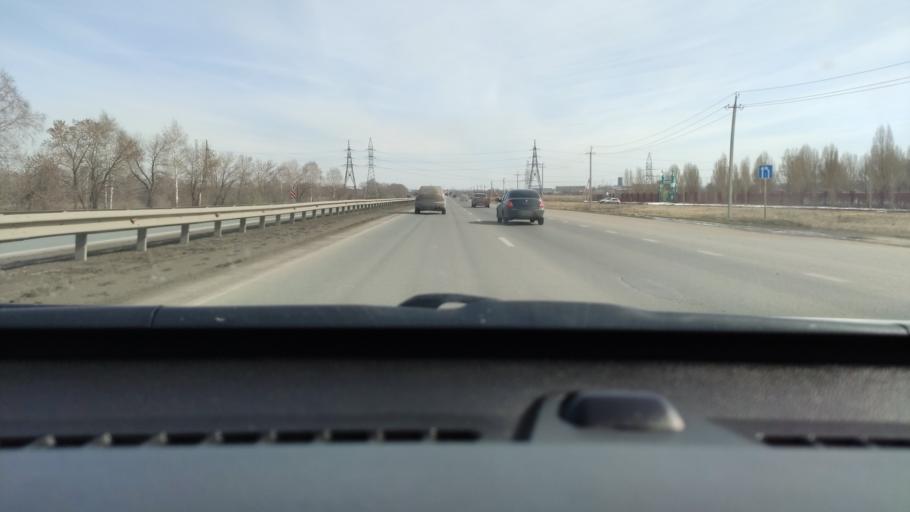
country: RU
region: Samara
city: Tol'yatti
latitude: 53.5776
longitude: 49.4150
